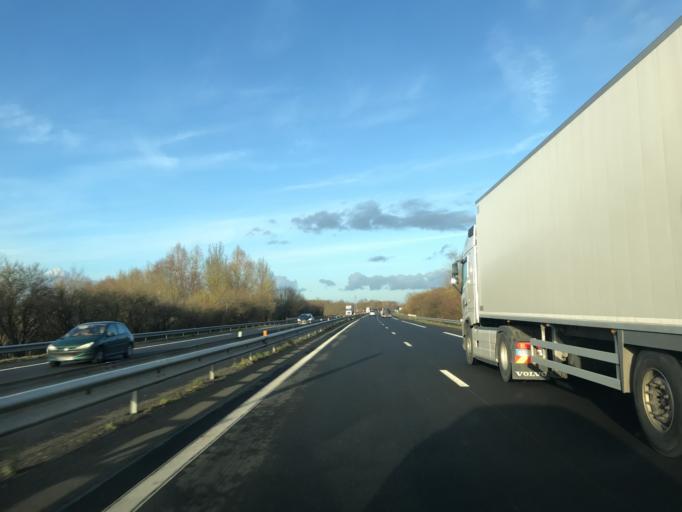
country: FR
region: Pays de la Loire
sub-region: Departement de la Sarthe
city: Vion
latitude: 47.7638
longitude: -0.2274
